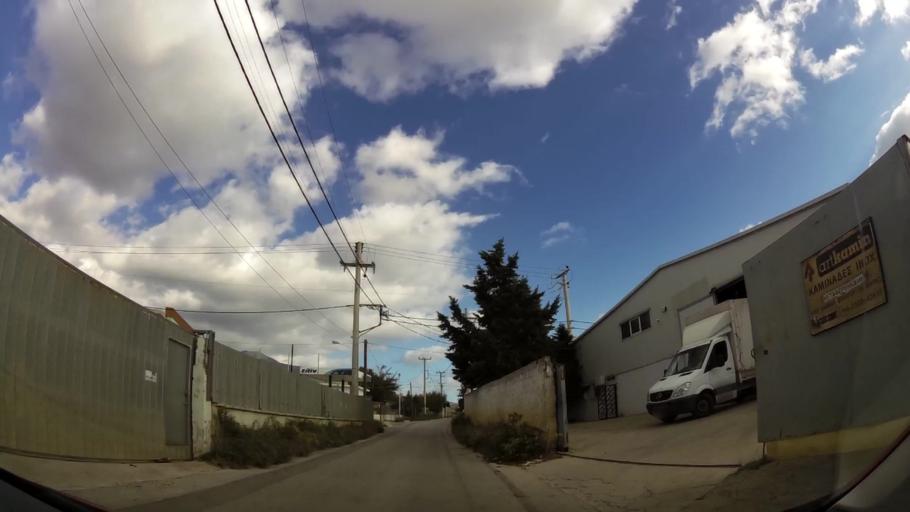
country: GR
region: Attica
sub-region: Nomarchia Anatolikis Attikis
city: Thrakomakedones
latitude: 38.1041
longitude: 23.7554
